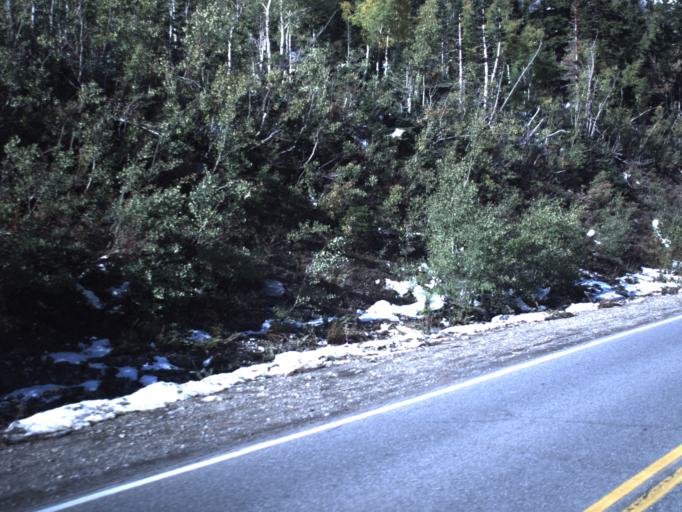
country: US
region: Utah
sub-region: Summit County
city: Snyderville
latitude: 40.5884
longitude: -111.6486
